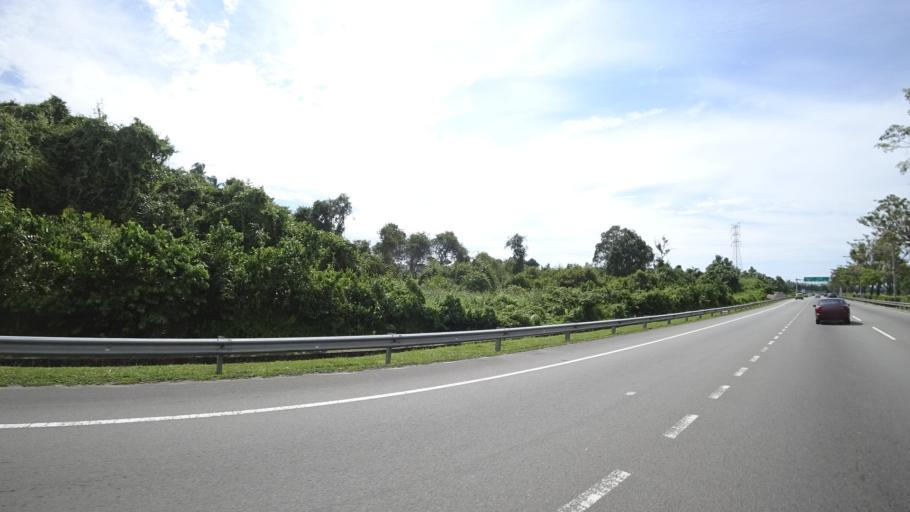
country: BN
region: Brunei and Muara
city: Bandar Seri Begawan
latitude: 4.9194
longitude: 114.9218
